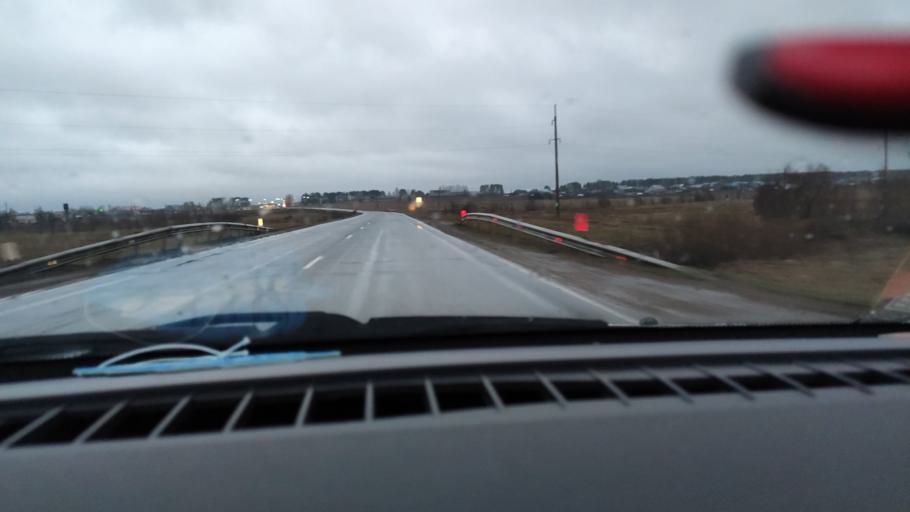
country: RU
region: Udmurtiya
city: Alnashi
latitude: 56.1846
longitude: 52.4584
